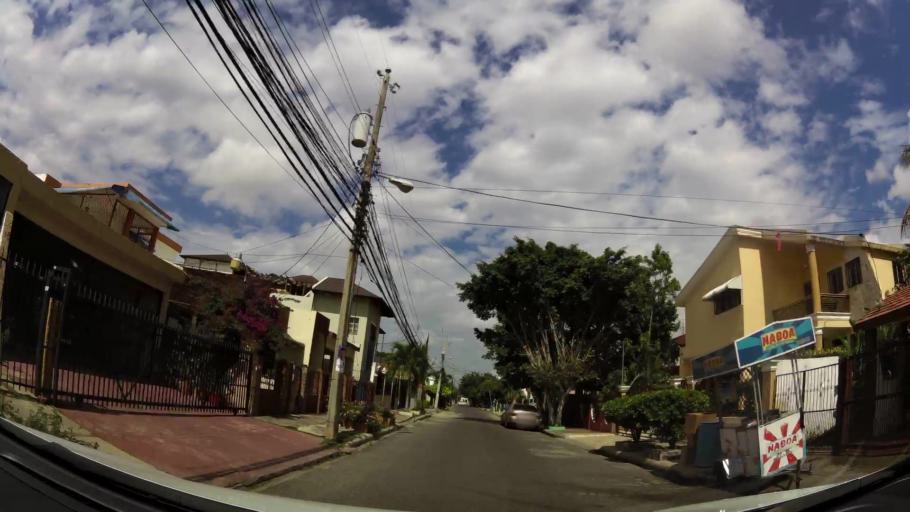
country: DO
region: Santiago
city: Santiago de los Caballeros
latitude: 19.4710
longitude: -70.6931
